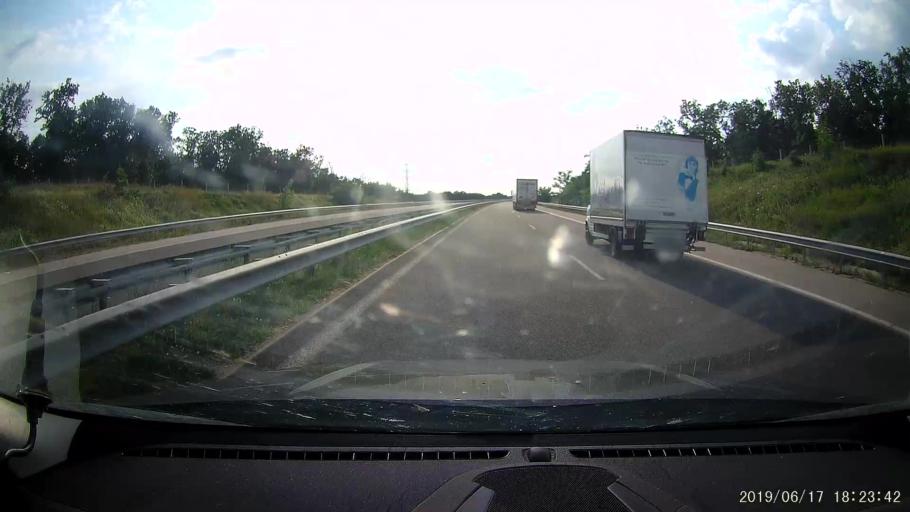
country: BG
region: Khaskovo
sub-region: Obshtina Simeonovgrad
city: Simeonovgrad
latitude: 41.9770
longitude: 25.7130
